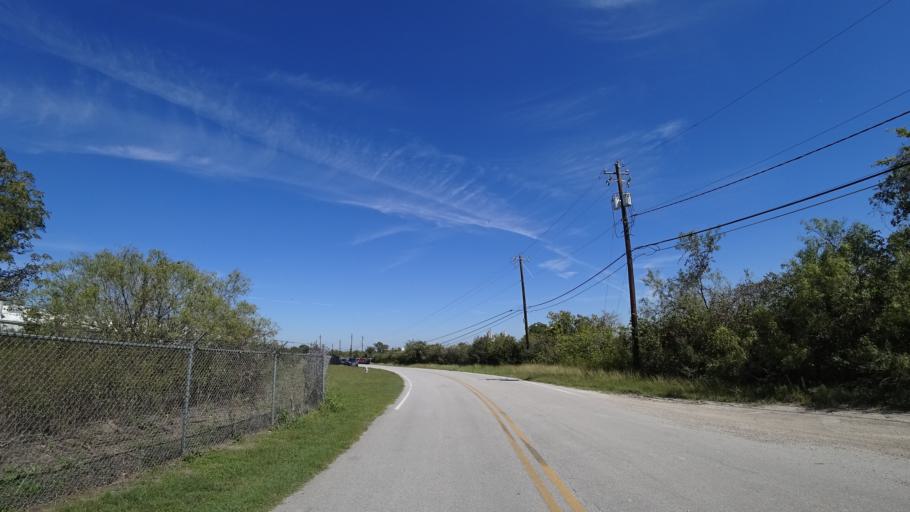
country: US
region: Texas
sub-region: Travis County
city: Austin
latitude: 30.1852
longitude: -97.7063
